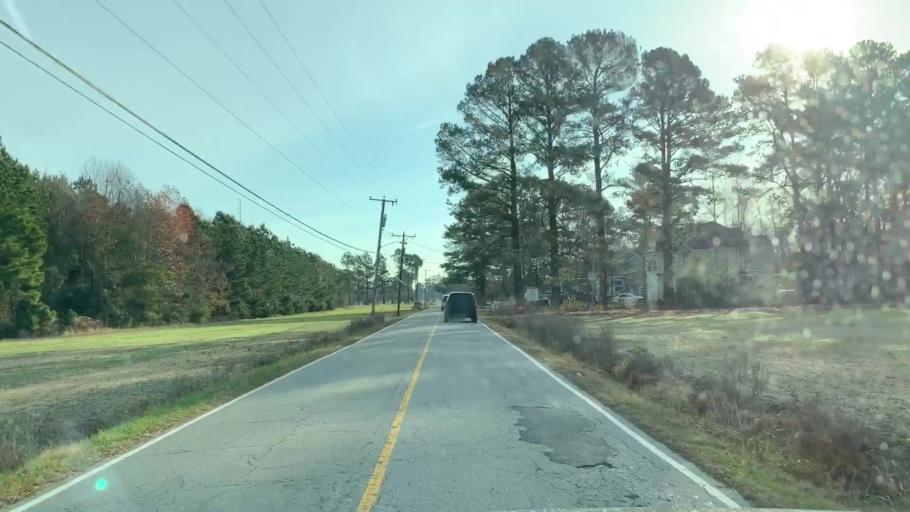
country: US
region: Virginia
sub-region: City of Virginia Beach
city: Virginia Beach
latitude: 36.6928
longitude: -76.0198
